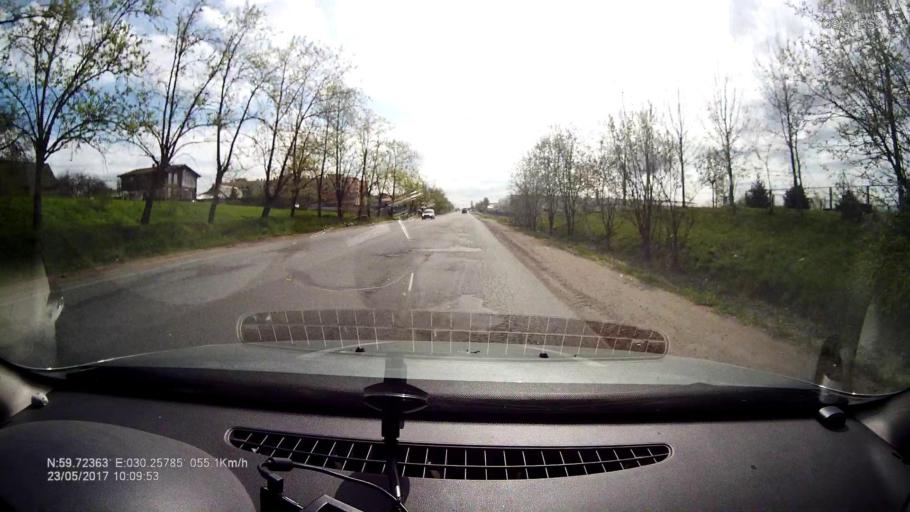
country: RU
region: St.-Petersburg
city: Aleksandrovskaya
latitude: 59.7236
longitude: 30.2582
